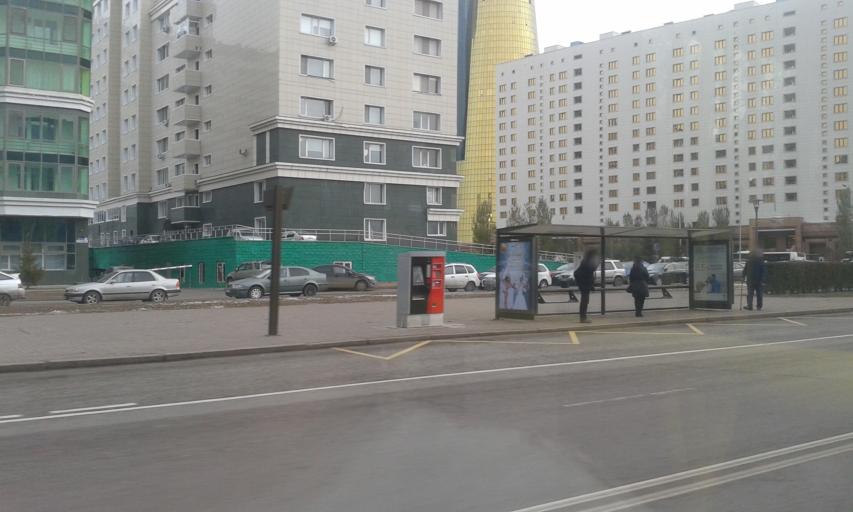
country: KZ
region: Astana Qalasy
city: Astana
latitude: 51.1250
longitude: 71.4361
